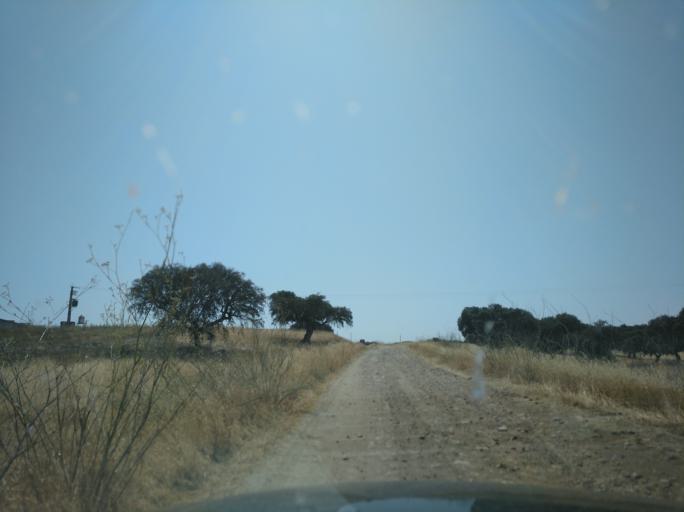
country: PT
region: Portalegre
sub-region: Campo Maior
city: Campo Maior
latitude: 39.0302
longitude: -6.9793
